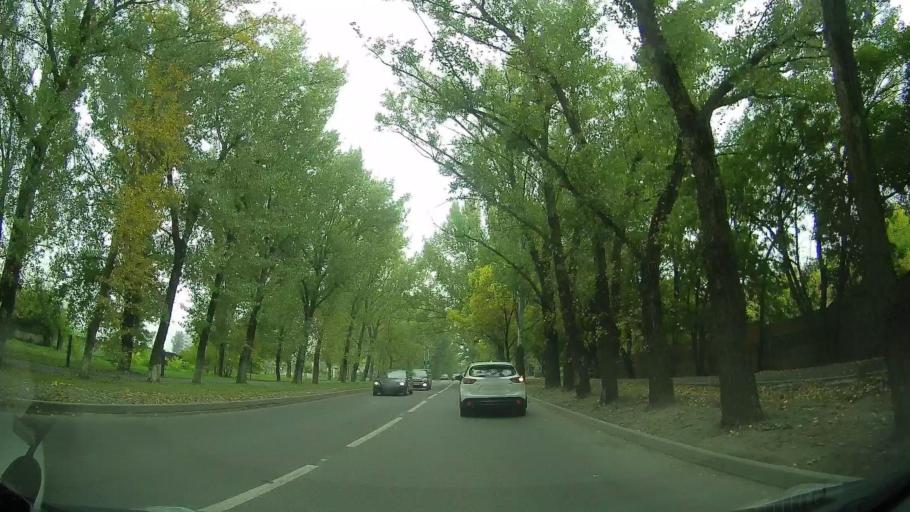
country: RU
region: Rostov
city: Severnyy
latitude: 47.2716
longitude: 39.6646
